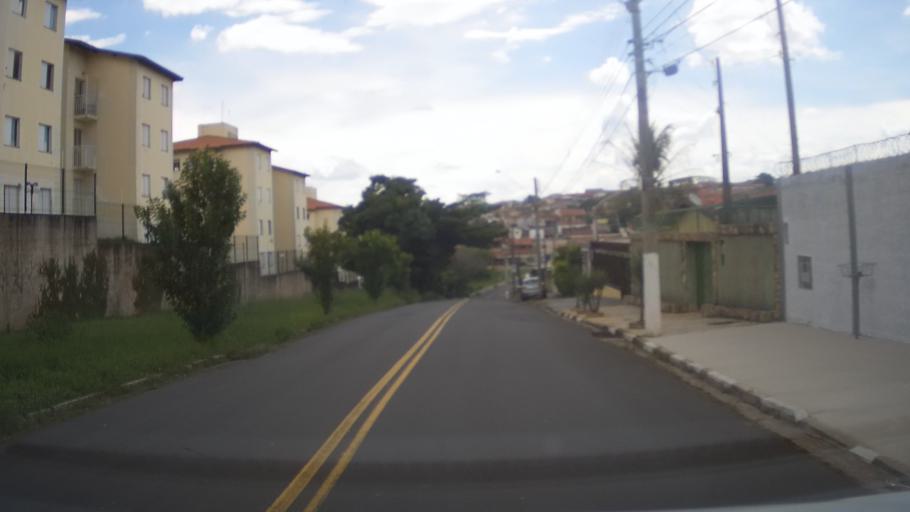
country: BR
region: Sao Paulo
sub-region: Campinas
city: Campinas
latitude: -22.9254
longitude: -47.0190
